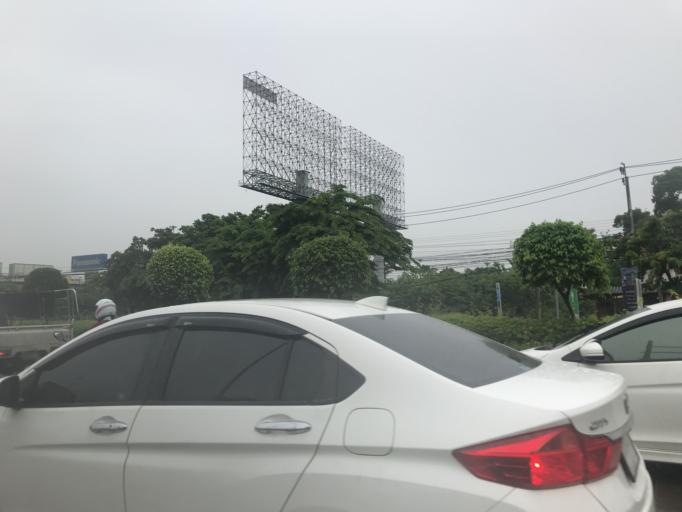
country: TH
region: Bangkok
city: Bueng Kum
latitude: 13.7924
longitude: 100.6846
